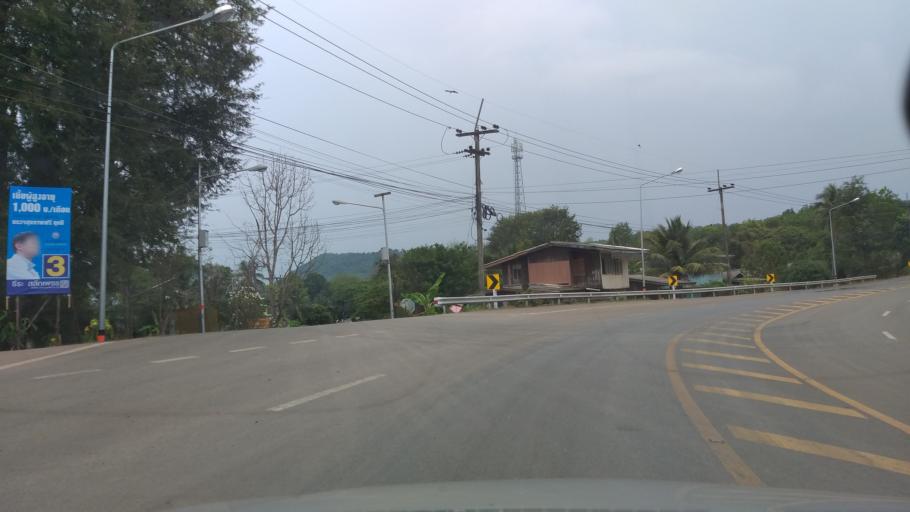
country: TH
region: Trat
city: Laem Ngop
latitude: 12.2579
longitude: 102.2863
